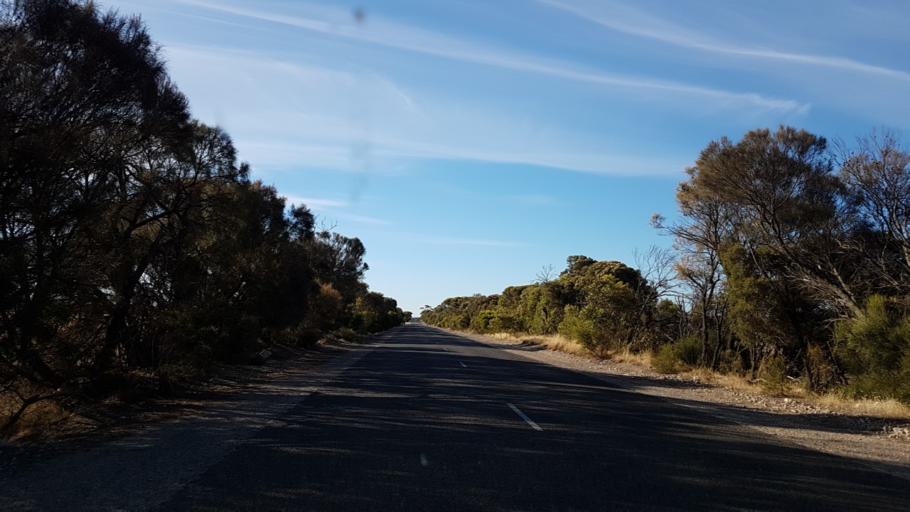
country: AU
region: South Australia
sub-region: Yorke Peninsula
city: Honiton
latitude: -34.9554
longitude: 137.1019
